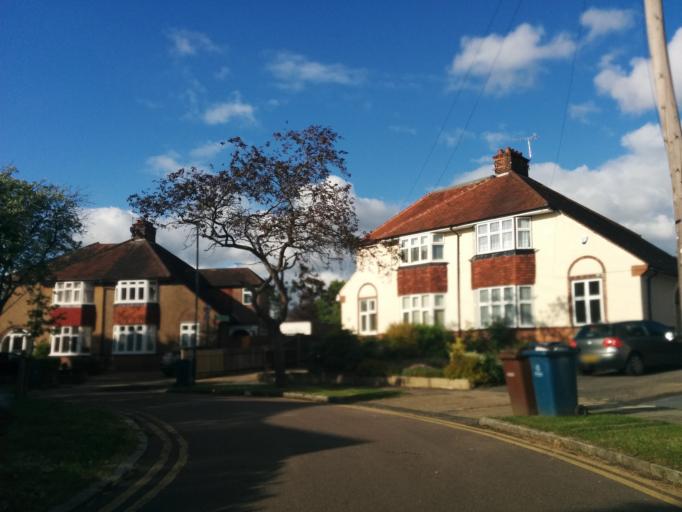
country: GB
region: England
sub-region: Greater London
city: Greenhill
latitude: 51.5720
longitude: -0.3500
